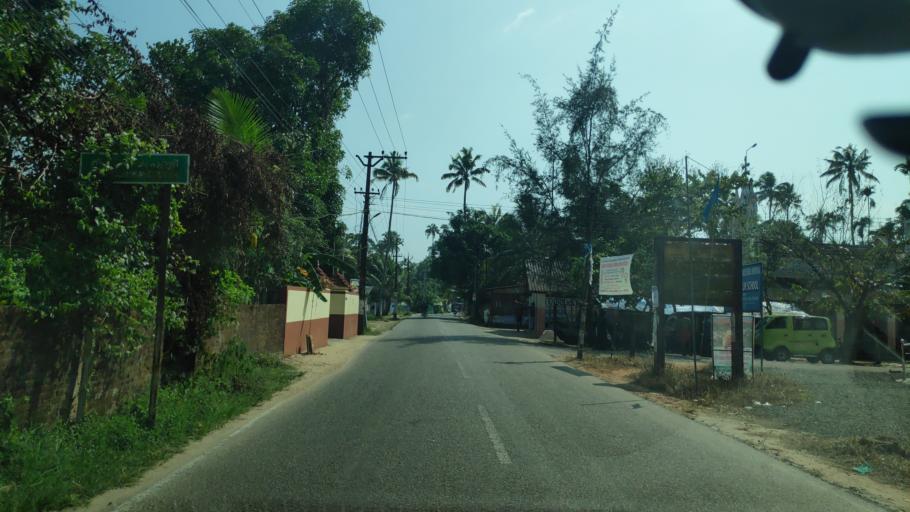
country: IN
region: Kerala
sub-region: Alappuzha
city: Vayalar
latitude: 9.6505
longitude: 76.2999
